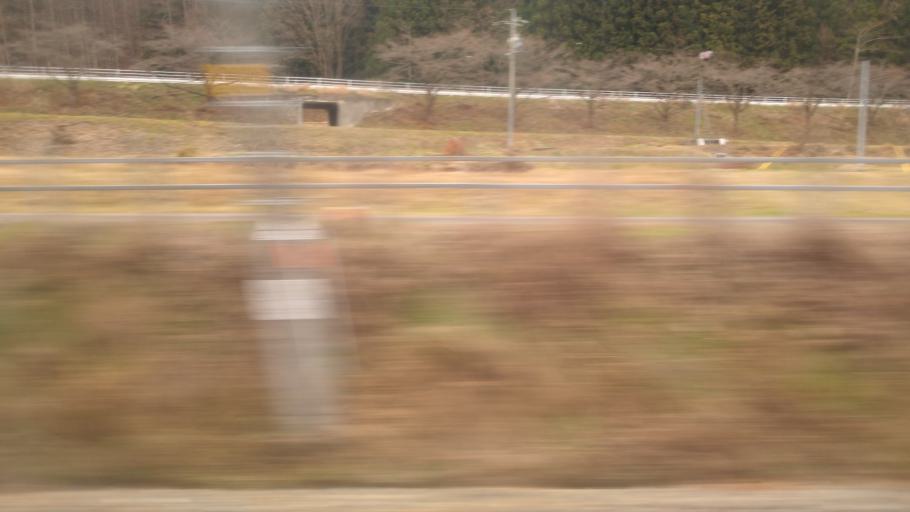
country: JP
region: Nagano
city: Shiojiri
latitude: 36.0531
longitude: 137.8971
